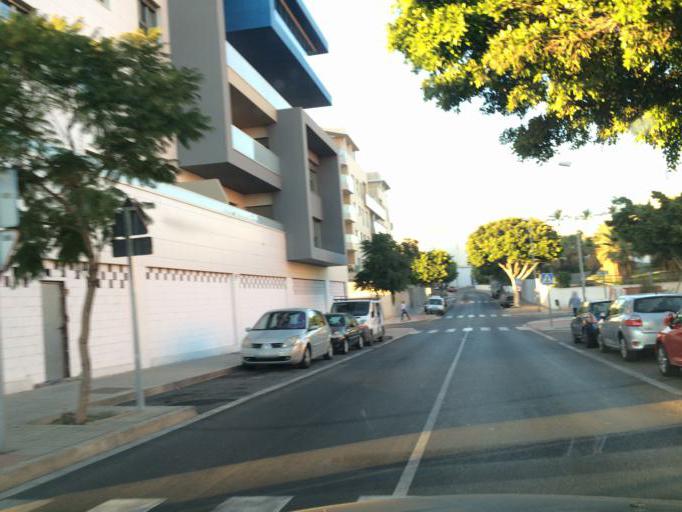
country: ES
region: Andalusia
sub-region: Provincia de Almeria
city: Almeria
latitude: 36.8518
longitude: -2.4483
